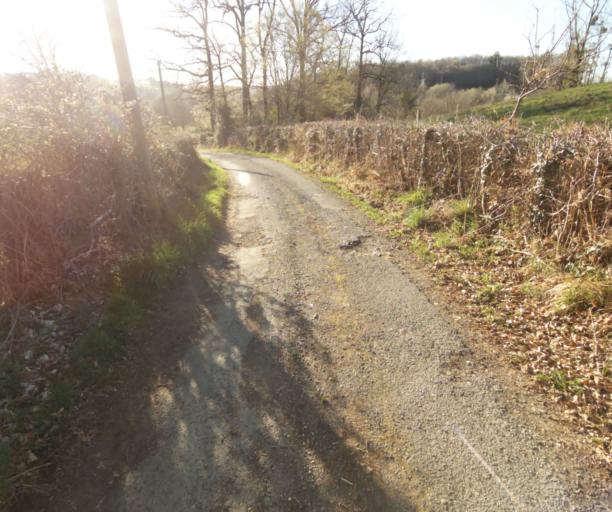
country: FR
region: Limousin
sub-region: Departement de la Correze
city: Seilhac
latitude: 45.3565
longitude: 1.7033
